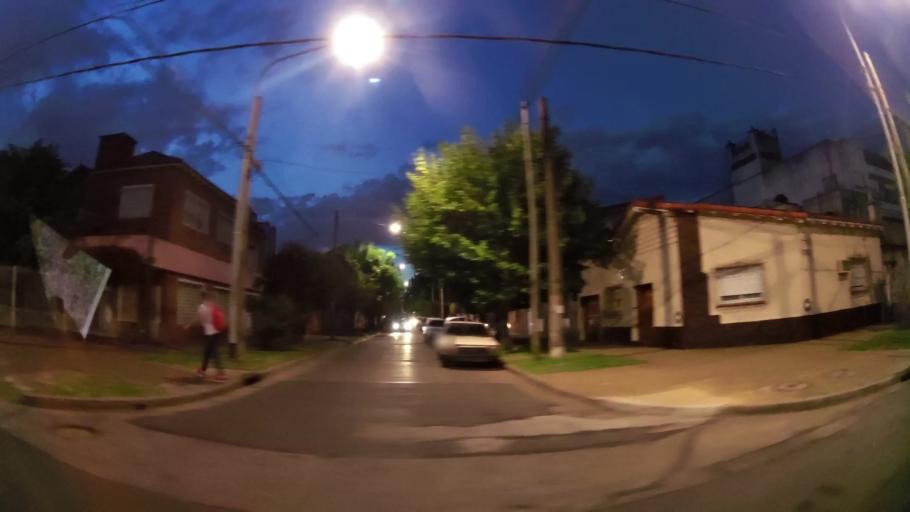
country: AR
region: Buenos Aires
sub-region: Partido de Avellaneda
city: Avellaneda
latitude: -34.7012
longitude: -58.3165
